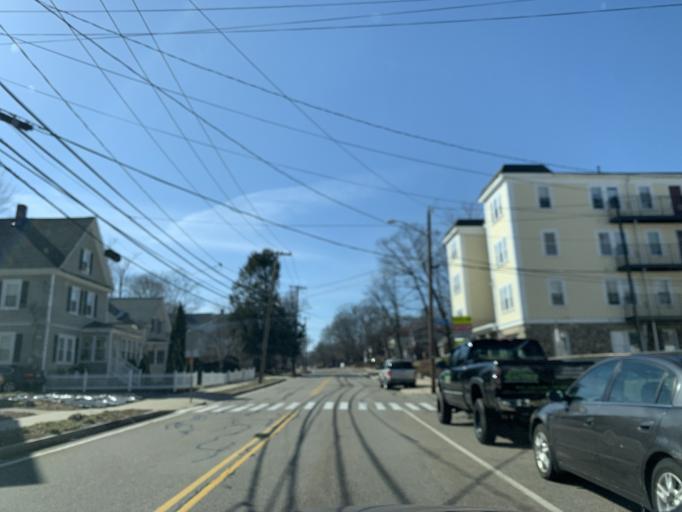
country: US
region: Massachusetts
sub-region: Norfolk County
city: Norwood
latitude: 42.1826
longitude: -71.2061
